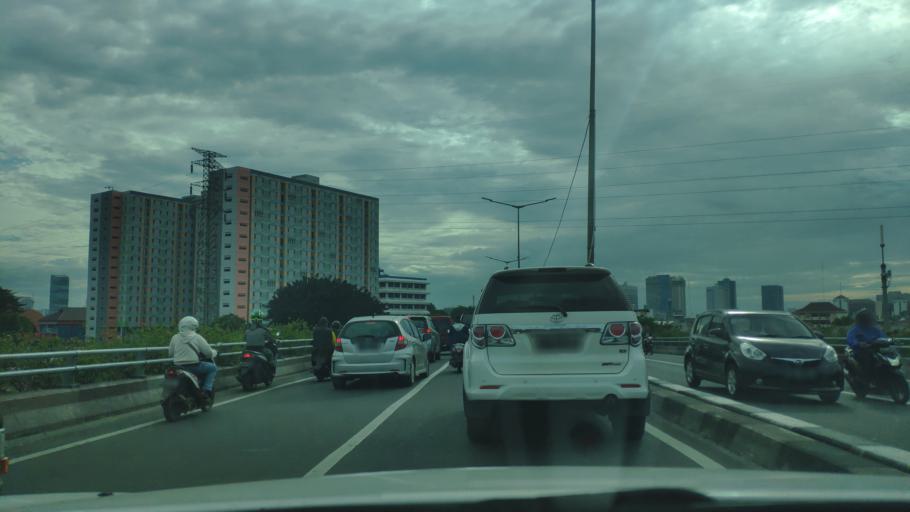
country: ID
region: Jakarta Raya
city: Jakarta
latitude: -6.1848
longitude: 106.8108
